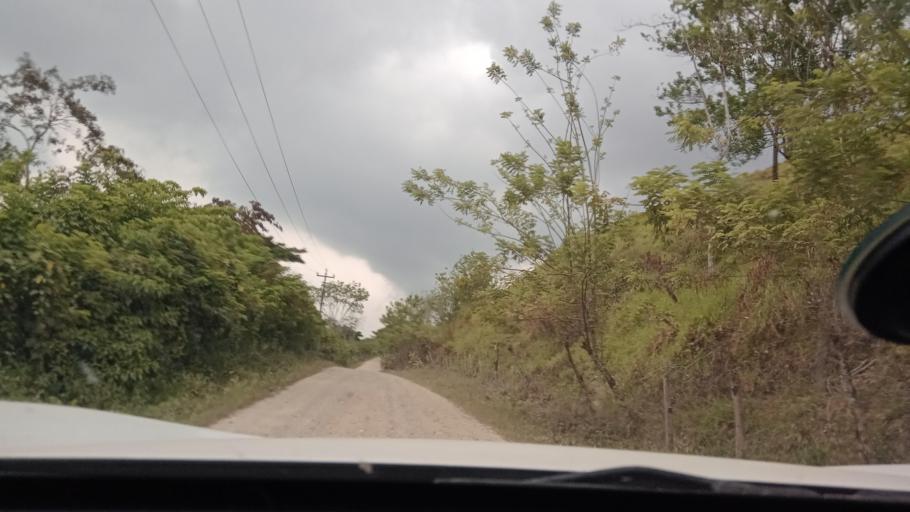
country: MX
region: Tabasco
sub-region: Huimanguillo
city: Francisco Rueda
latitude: 17.4399
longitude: -94.0638
